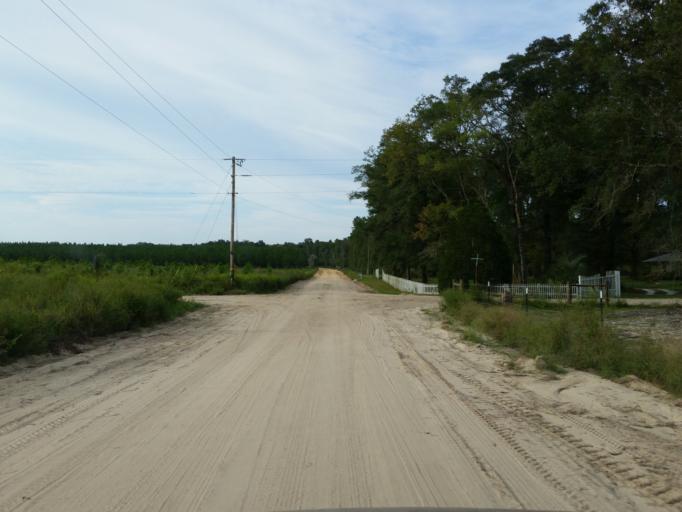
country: US
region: Florida
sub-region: Madison County
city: Madison
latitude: 30.5371
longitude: -83.2158
